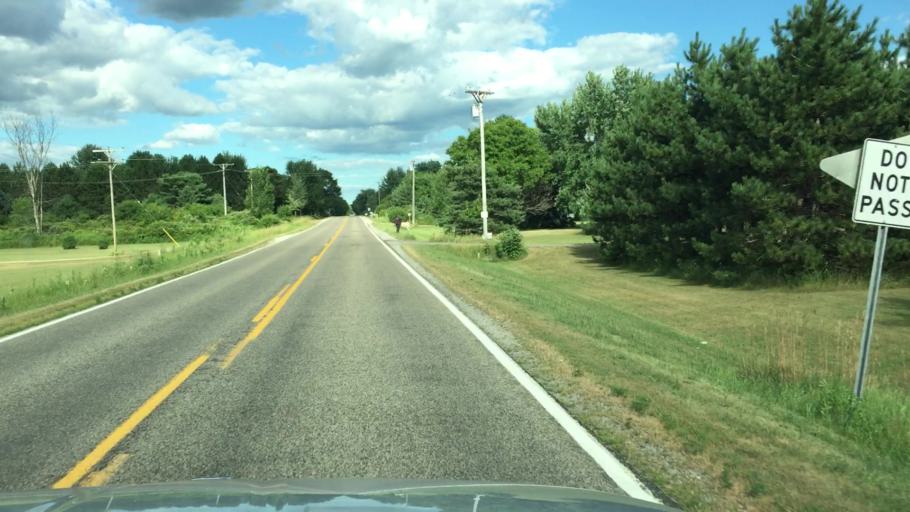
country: US
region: Michigan
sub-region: Saint Clair County
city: Yale
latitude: 43.1288
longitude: -82.8415
